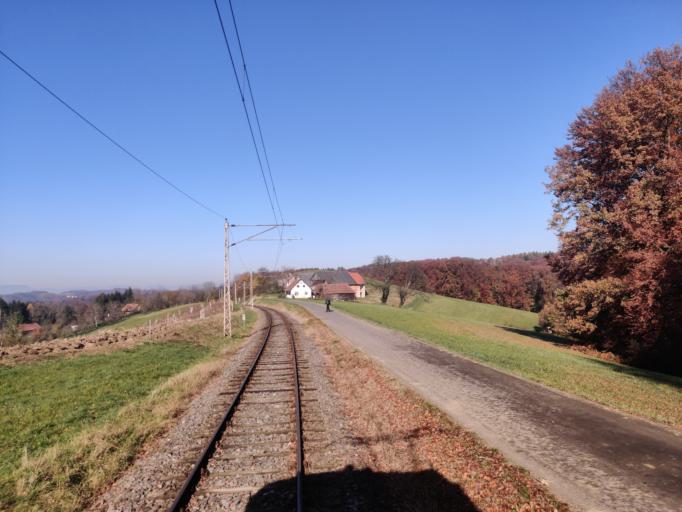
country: AT
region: Styria
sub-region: Politischer Bezirk Suedoststeiermark
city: Maierdorf
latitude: 46.8951
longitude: 15.8342
